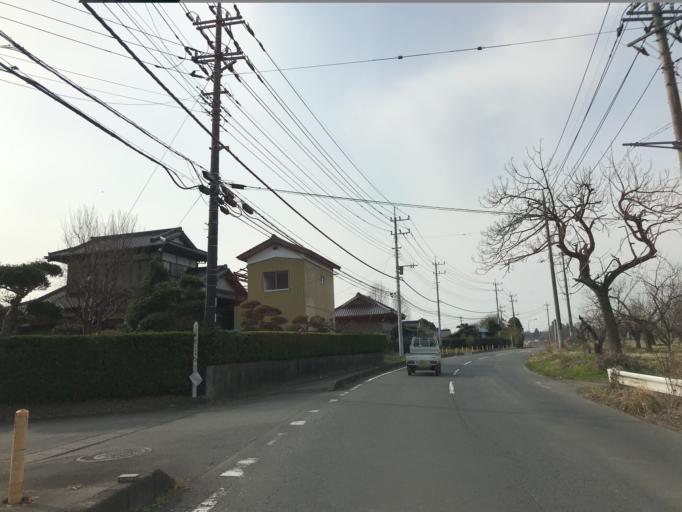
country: JP
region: Ibaraki
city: Okunoya
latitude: 36.2351
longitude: 140.3688
